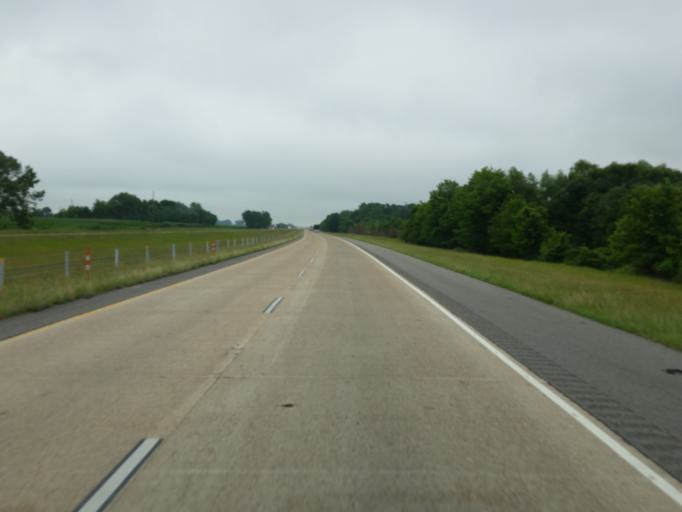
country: US
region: Louisiana
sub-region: Madison Parish
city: Tallulah
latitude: 32.3353
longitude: -91.0576
